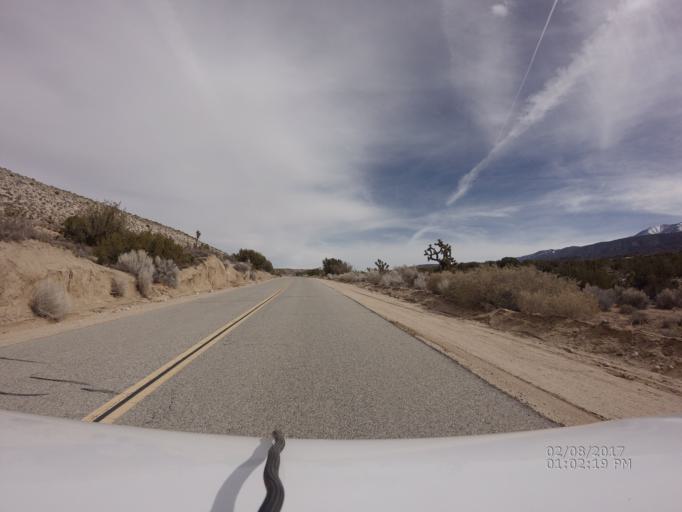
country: US
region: California
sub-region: Los Angeles County
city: Lake Los Angeles
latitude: 34.4496
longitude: -117.8249
